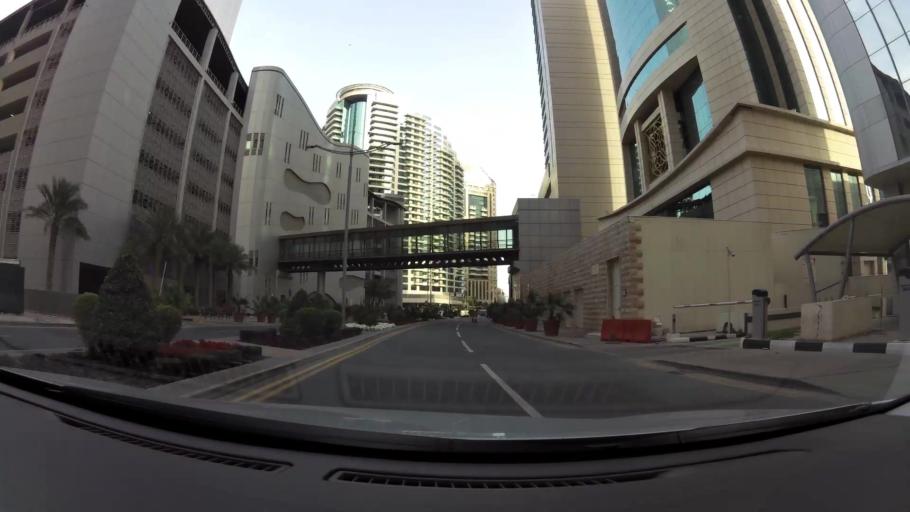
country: QA
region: Baladiyat ad Dawhah
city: Doha
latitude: 25.3268
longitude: 51.5335
